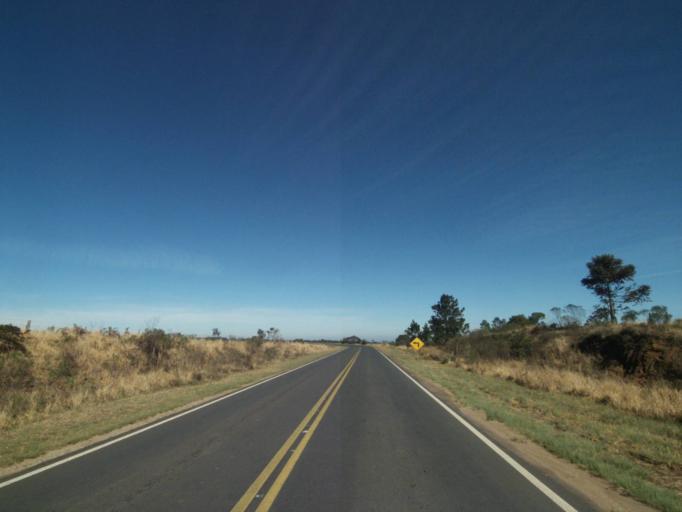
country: BR
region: Parana
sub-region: Tibagi
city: Tibagi
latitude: -24.6406
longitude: -50.2326
